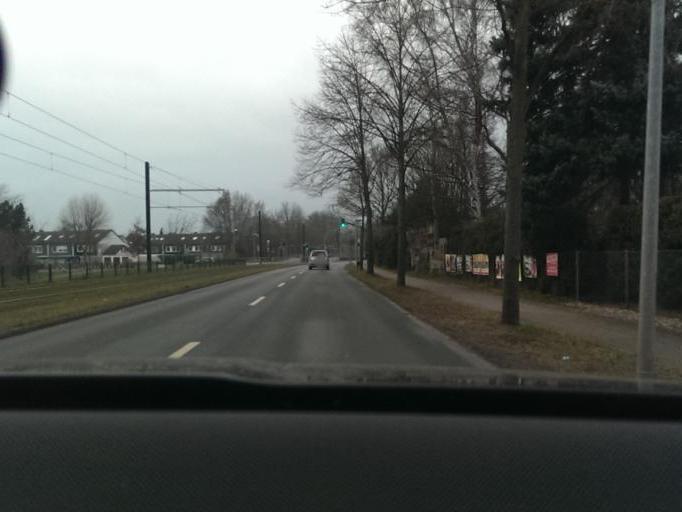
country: DE
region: Lower Saxony
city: Isernhagen Farster Bauerschaft
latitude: 52.4298
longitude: 9.8472
